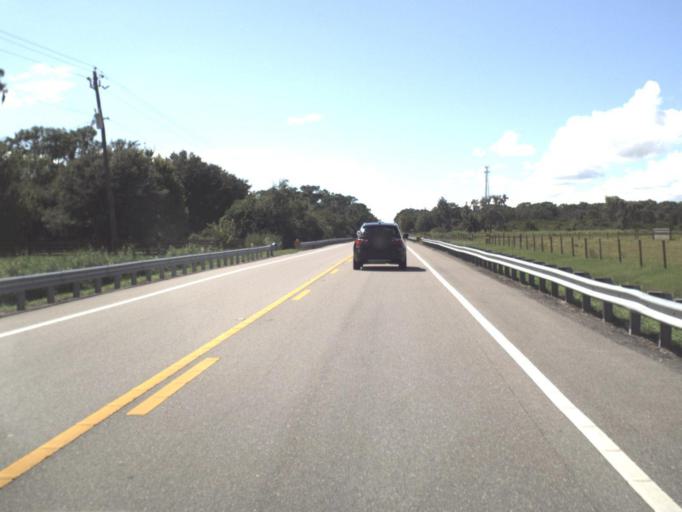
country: US
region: Florida
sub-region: Sarasota County
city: Lake Sarasota
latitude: 27.3872
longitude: -82.2560
